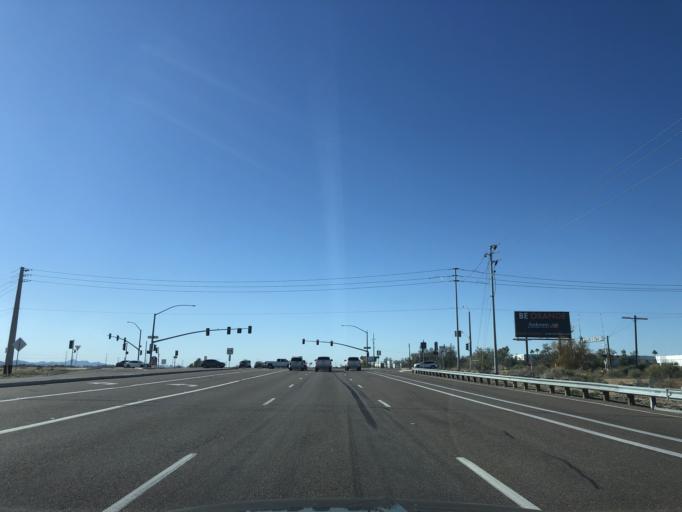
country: US
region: Arizona
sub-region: Maricopa County
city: Goodyear
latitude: 33.4047
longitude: -112.4255
